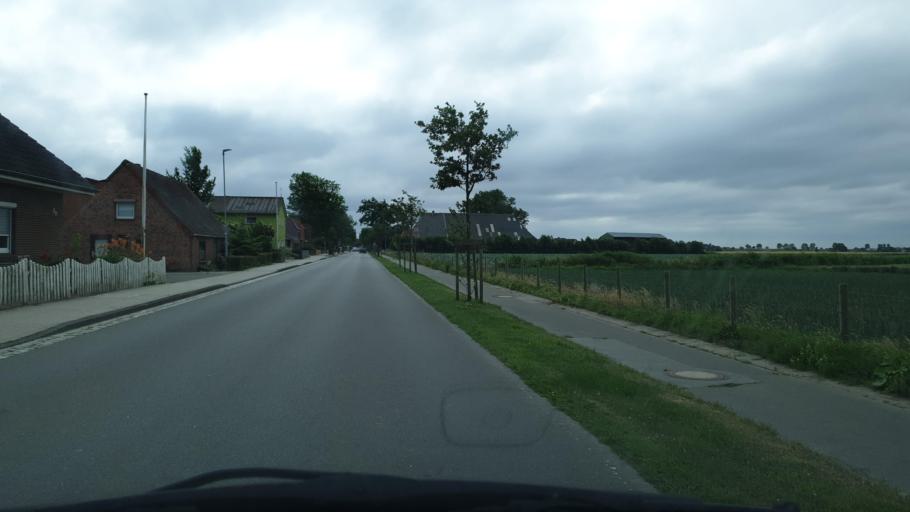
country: DE
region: Schleswig-Holstein
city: Friedrichskoog
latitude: 54.0122
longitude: 8.8934
